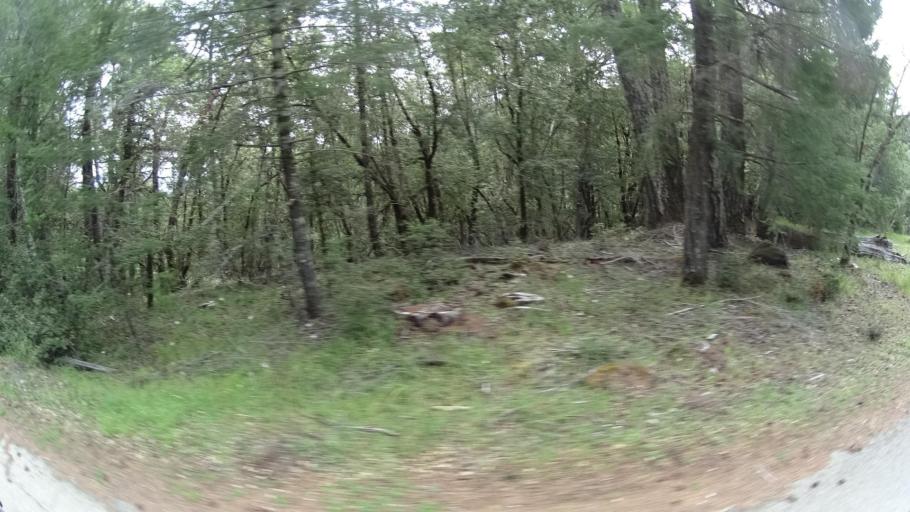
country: US
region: California
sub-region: Humboldt County
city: Redway
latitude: 40.0574
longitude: -123.8328
